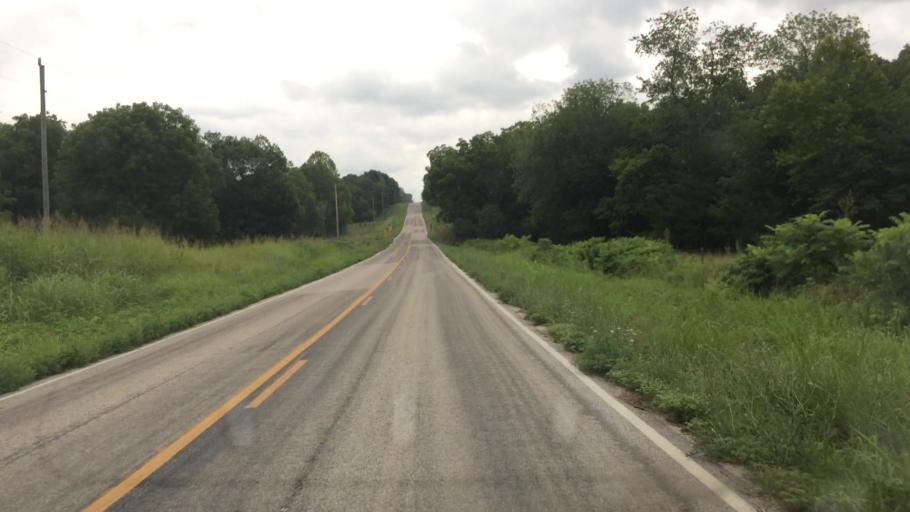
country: US
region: Missouri
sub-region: Webster County
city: Marshfield
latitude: 37.3415
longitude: -93.0152
